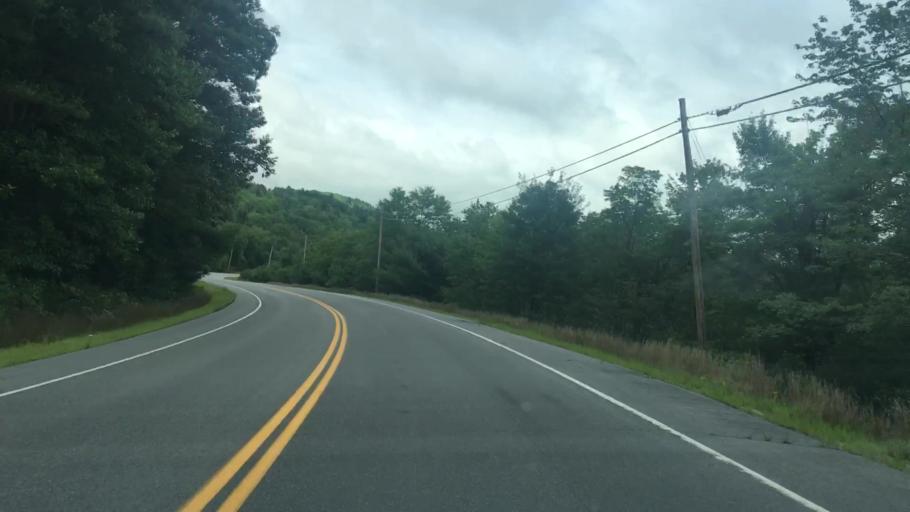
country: US
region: Maine
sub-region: York County
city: Cornish
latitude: 43.7775
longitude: -70.8242
